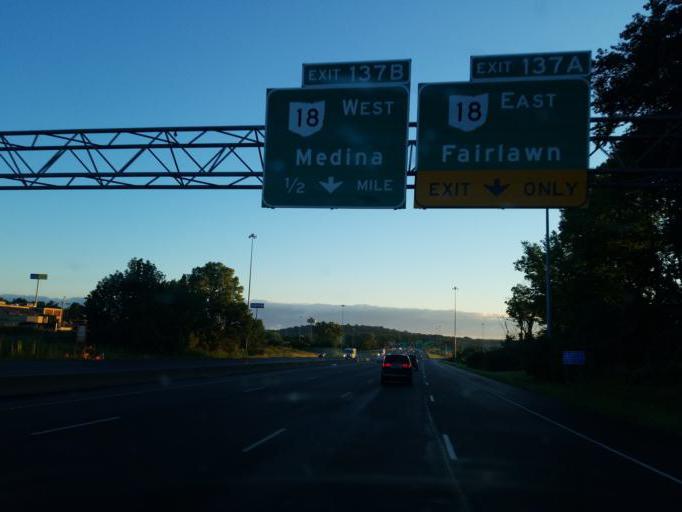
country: US
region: Ohio
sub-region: Summit County
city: Montrose-Ghent
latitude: 41.1295
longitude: -81.6520
